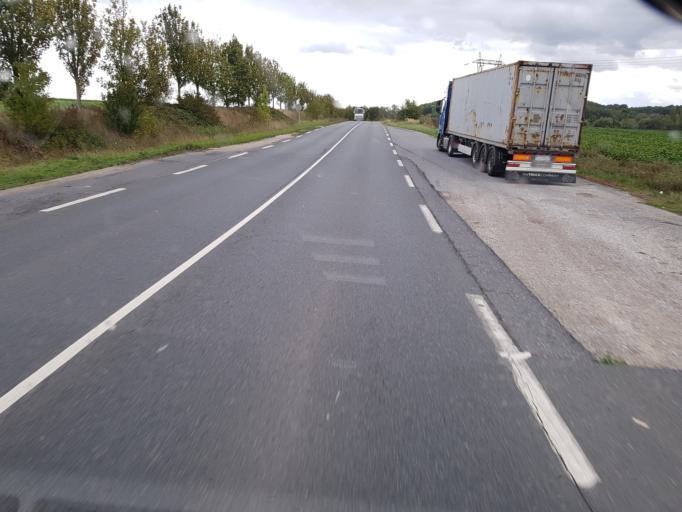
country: FR
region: Ile-de-France
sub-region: Departement de Seine-et-Marne
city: Monthyon
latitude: 48.9987
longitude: 2.8498
